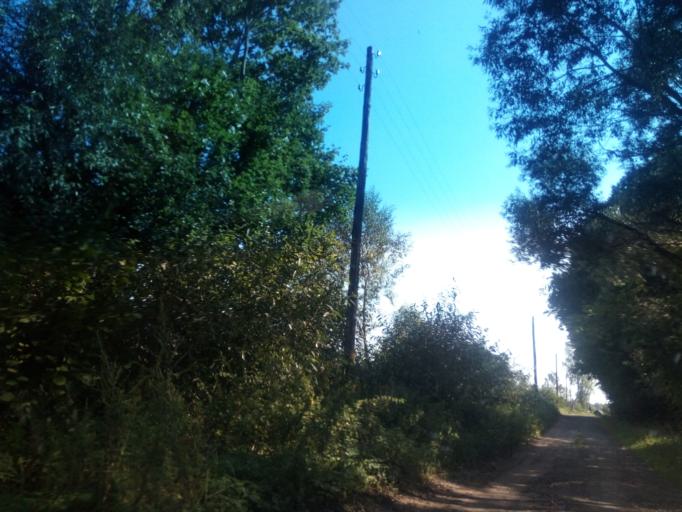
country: BY
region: Vitebsk
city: Dzisna
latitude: 55.6482
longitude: 28.2545
